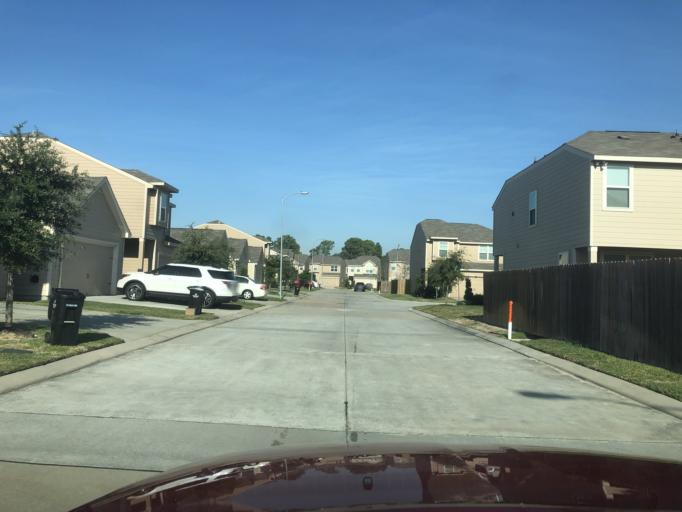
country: US
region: Texas
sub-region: Harris County
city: Spring
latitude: 30.0107
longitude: -95.4608
